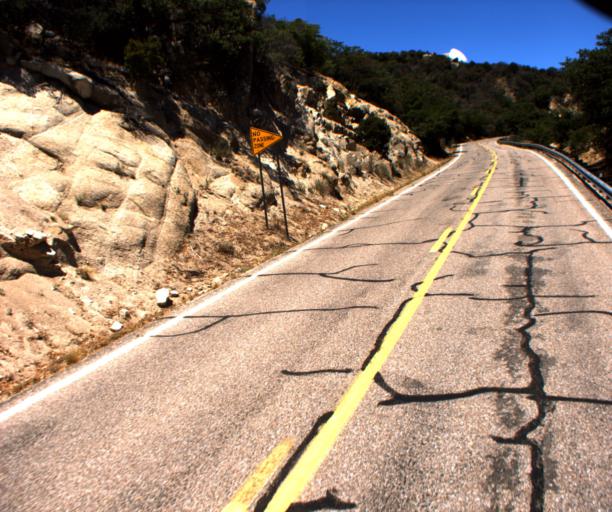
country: US
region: Arizona
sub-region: Pima County
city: Sells
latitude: 31.9497
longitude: -111.6138
